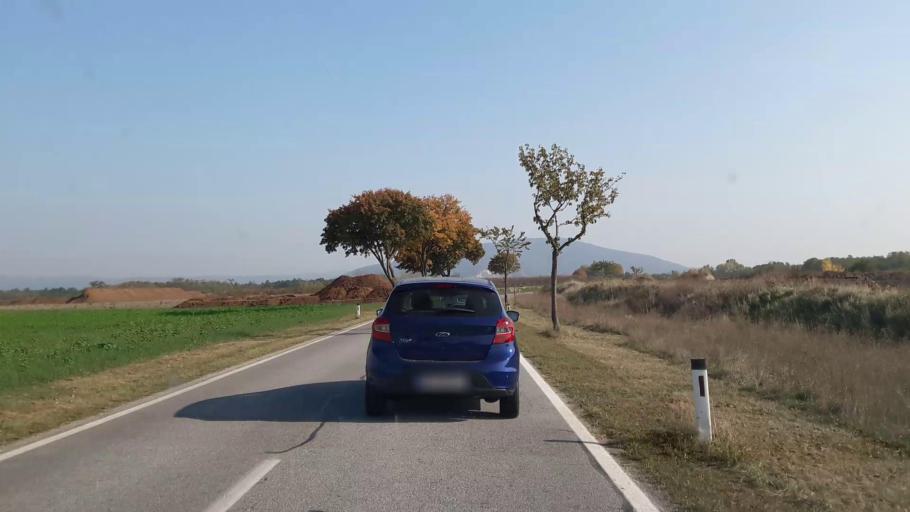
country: AT
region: Lower Austria
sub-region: Politischer Bezirk Ganserndorf
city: Marchegg
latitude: 48.2202
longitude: 16.9187
